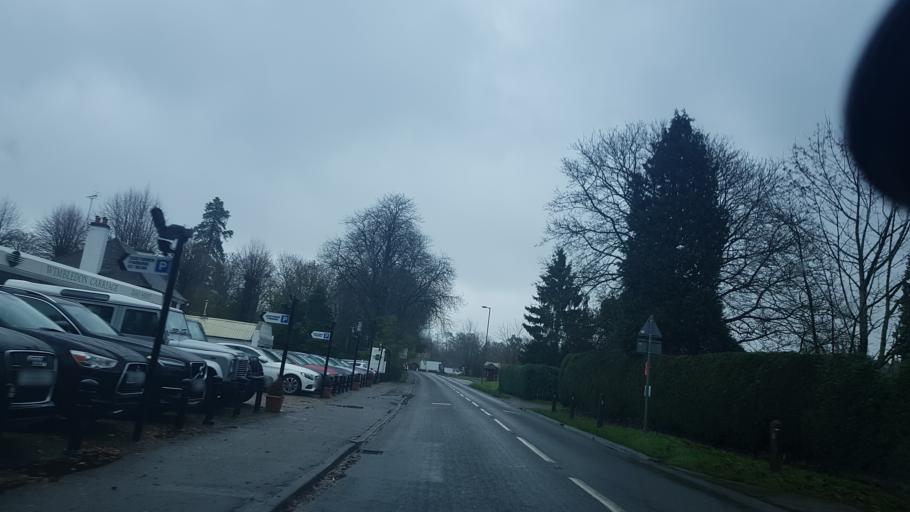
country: GB
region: England
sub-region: Surrey
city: East Horsley
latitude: 51.2626
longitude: -0.4348
